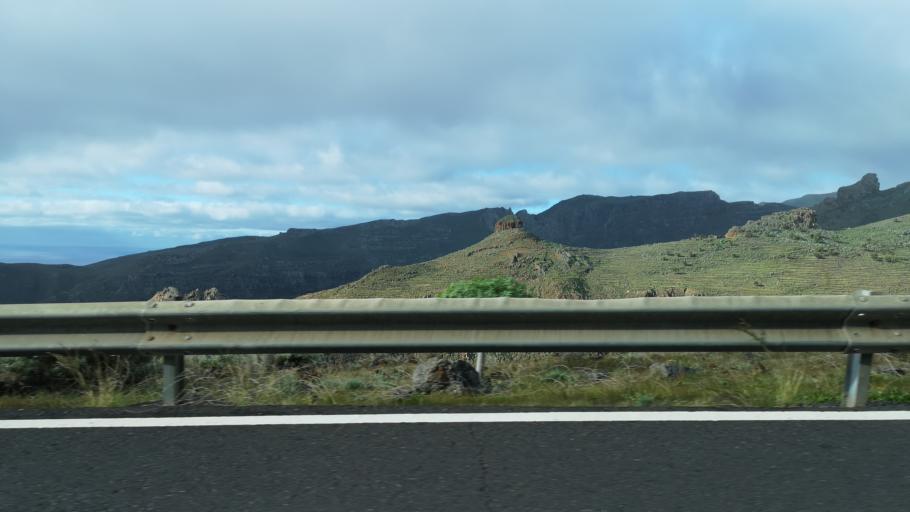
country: ES
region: Canary Islands
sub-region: Provincia de Santa Cruz de Tenerife
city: San Sebastian de la Gomera
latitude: 28.0933
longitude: -17.1532
